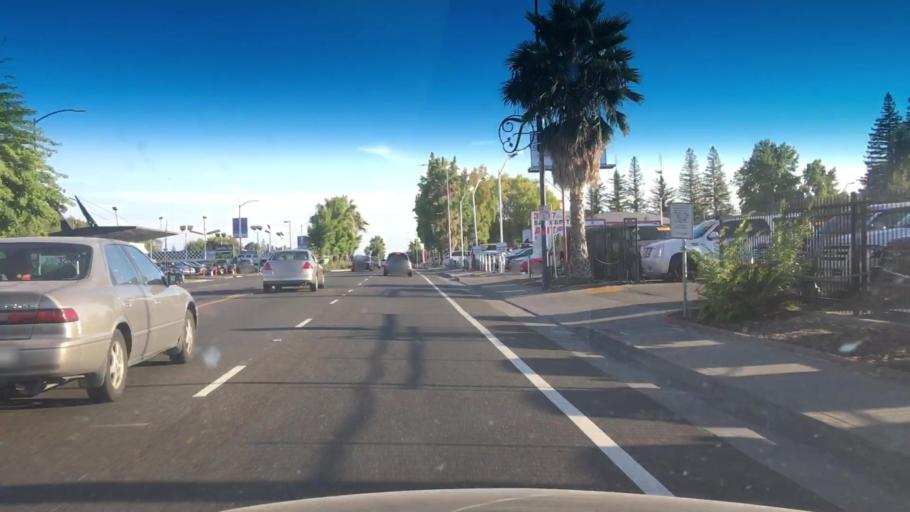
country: US
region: California
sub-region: Sacramento County
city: Arden-Arcade
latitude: 38.6257
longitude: -121.4015
